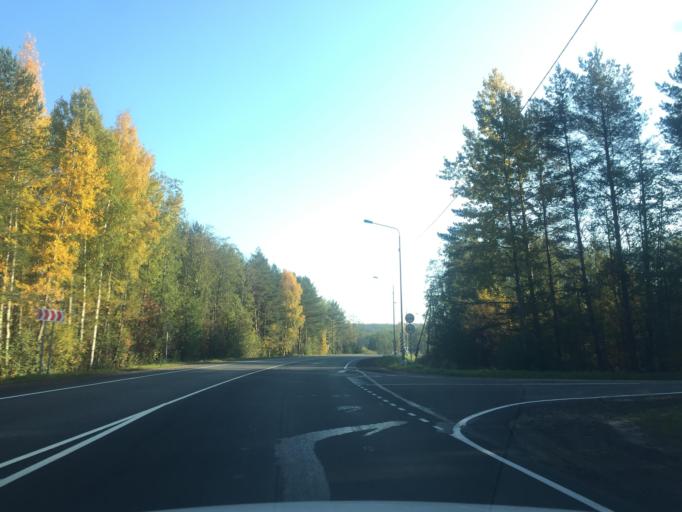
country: RU
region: Leningrad
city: Sapernoye
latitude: 60.7122
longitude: 29.9761
